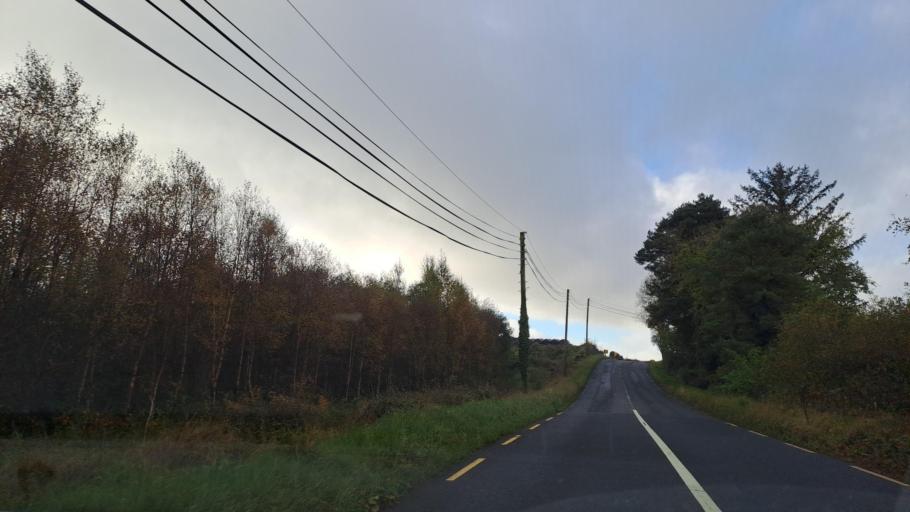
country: IE
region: Ulster
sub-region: An Cabhan
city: Virginia
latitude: 53.8527
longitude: -7.0517
